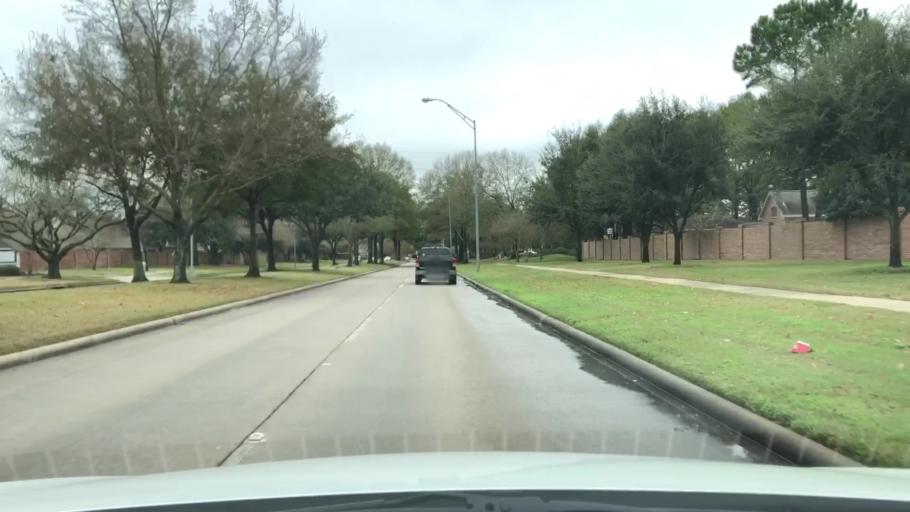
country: US
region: Texas
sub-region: Fort Bend County
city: Cinco Ranch
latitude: 29.7434
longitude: -95.7514
